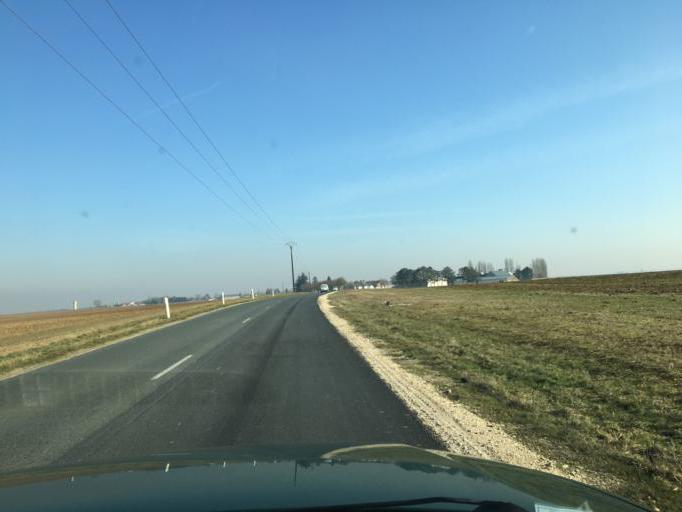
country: FR
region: Centre
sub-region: Departement du Loiret
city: Patay
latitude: 48.0532
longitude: 1.7181
